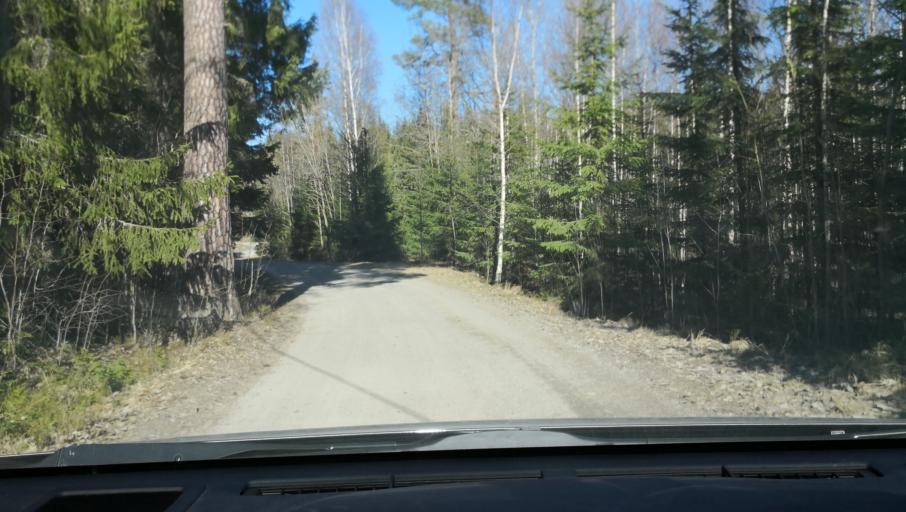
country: SE
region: Vaestmanland
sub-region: Sala Kommun
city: Sala
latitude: 59.9387
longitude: 16.4531
